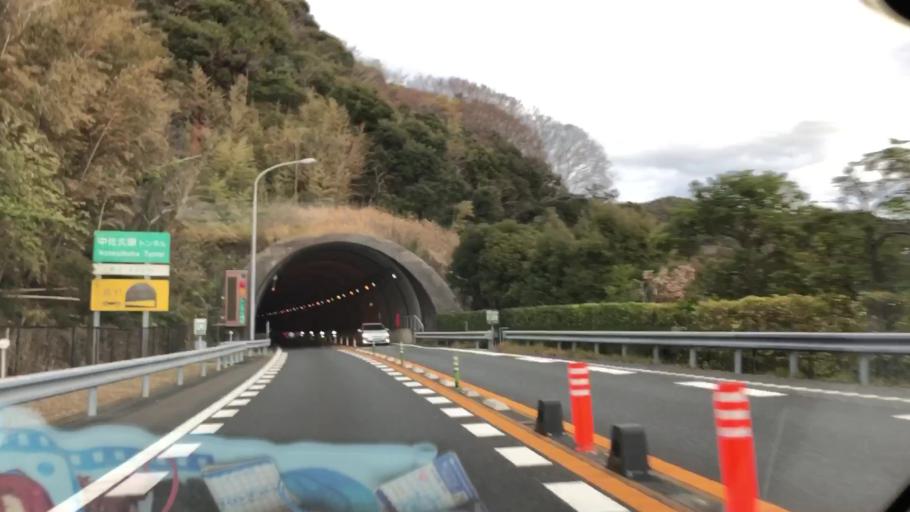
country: JP
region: Chiba
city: Tateyama
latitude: 35.1173
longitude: 139.8513
